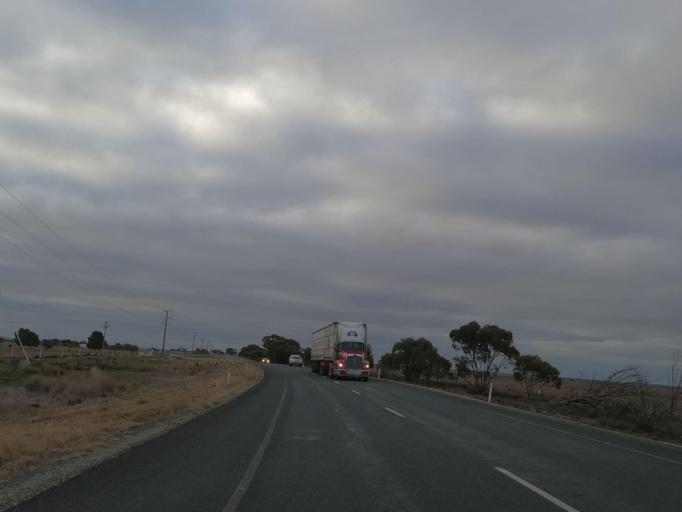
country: AU
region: Victoria
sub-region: Swan Hill
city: Swan Hill
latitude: -35.5842
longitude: 143.7902
